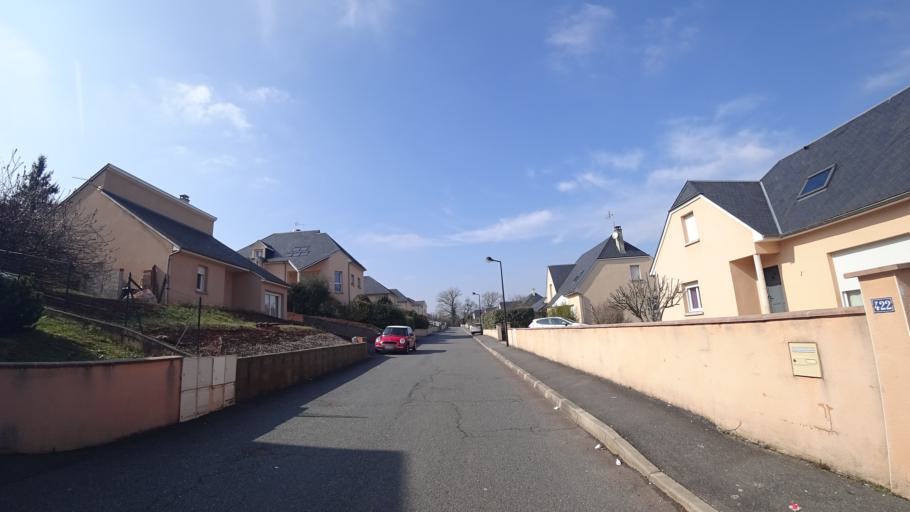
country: FR
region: Midi-Pyrenees
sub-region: Departement de l'Aveyron
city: Olemps
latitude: 44.3644
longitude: 2.5577
